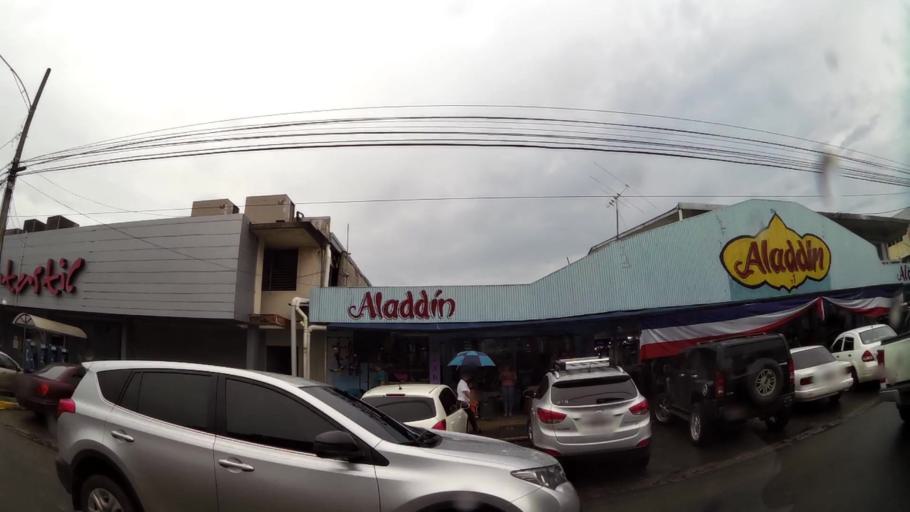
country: PA
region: Veraguas
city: Santiago de Veraguas
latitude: 8.0972
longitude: -80.9810
